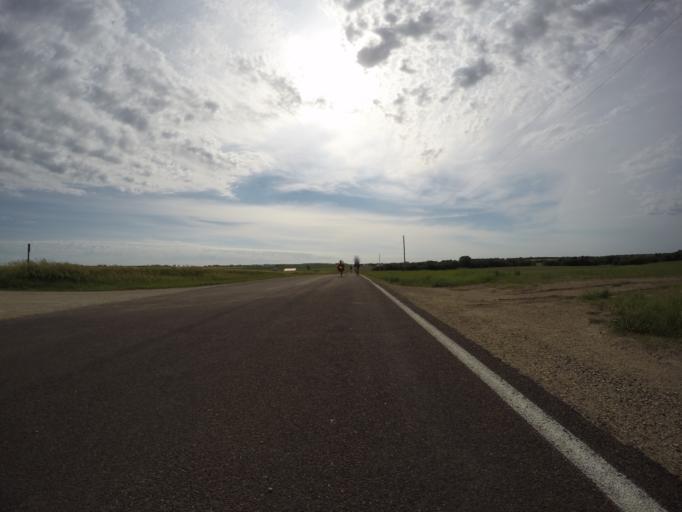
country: US
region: Kansas
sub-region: Republic County
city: Belleville
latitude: 39.7123
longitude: -97.3504
